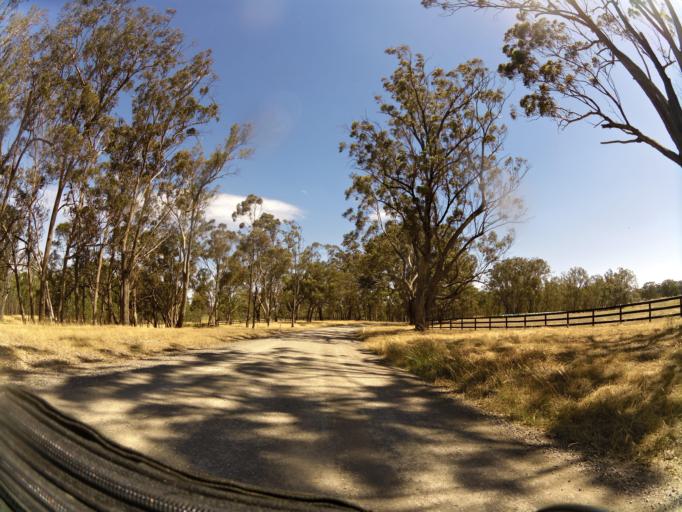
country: AU
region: Victoria
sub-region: Campaspe
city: Kyabram
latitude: -36.8285
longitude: 145.0778
